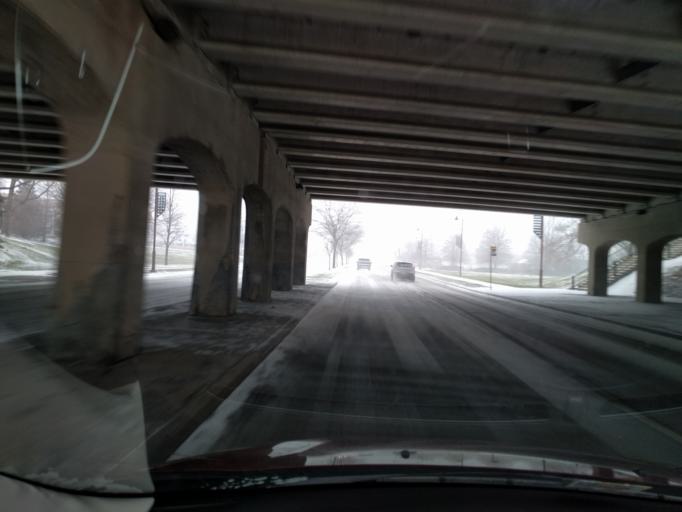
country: US
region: Wisconsin
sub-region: Milwaukee County
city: Glendale
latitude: 43.1190
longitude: -87.9352
